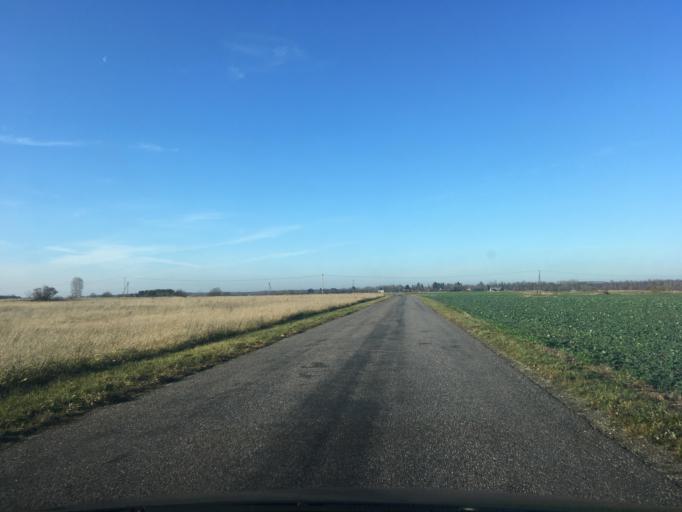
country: EE
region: Harju
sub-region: Maardu linn
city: Maardu
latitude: 59.4523
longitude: 25.1105
